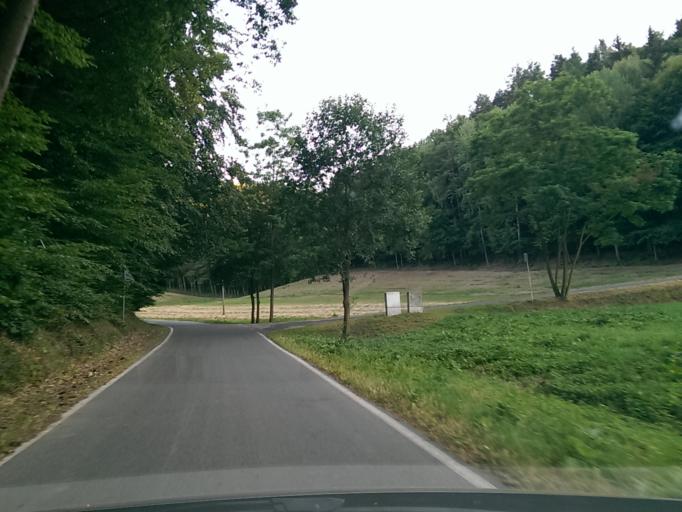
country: CZ
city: Duba
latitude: 50.4788
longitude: 14.5051
